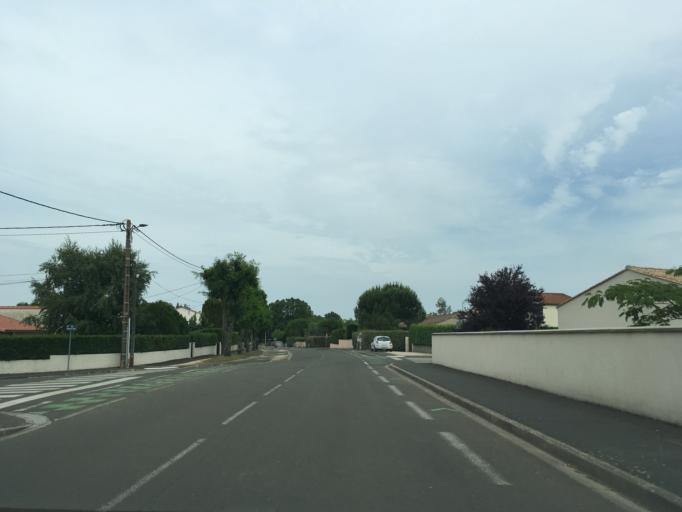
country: FR
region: Poitou-Charentes
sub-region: Departement des Deux-Sevres
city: Bessines
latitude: 46.3196
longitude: -0.5149
